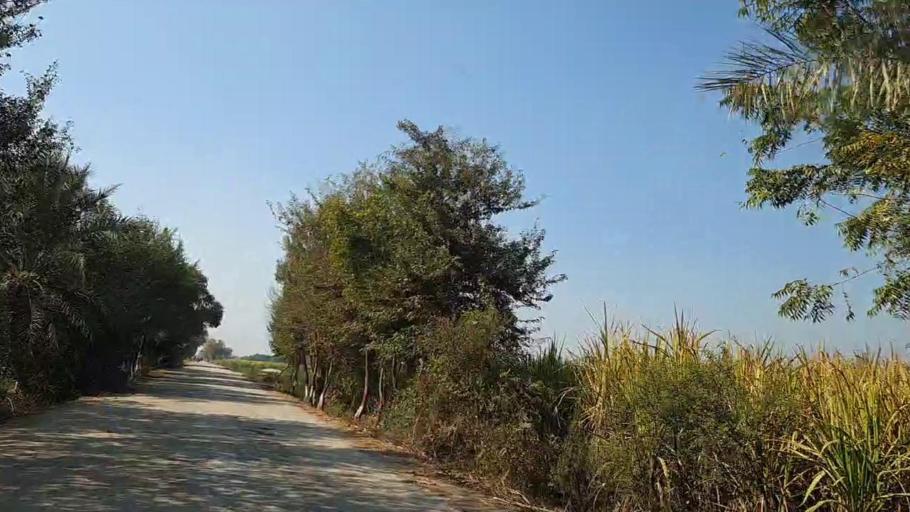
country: PK
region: Sindh
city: Sakrand
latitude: 26.2906
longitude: 68.0951
